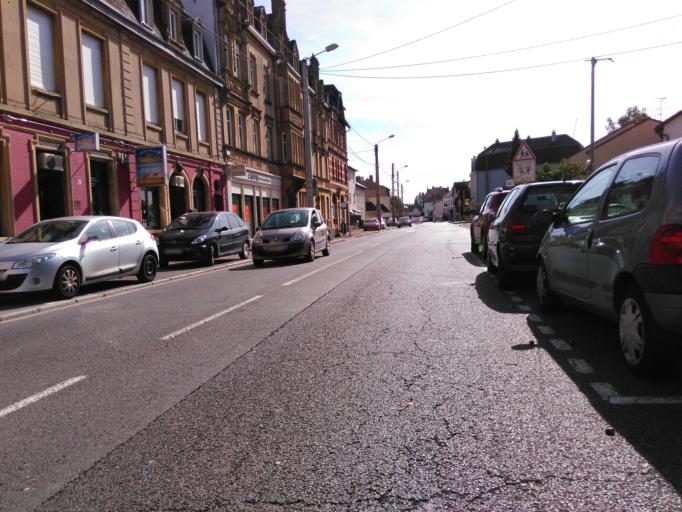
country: FR
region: Lorraine
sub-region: Departement de la Moselle
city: Thionville
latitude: 49.3702
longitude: 6.1692
